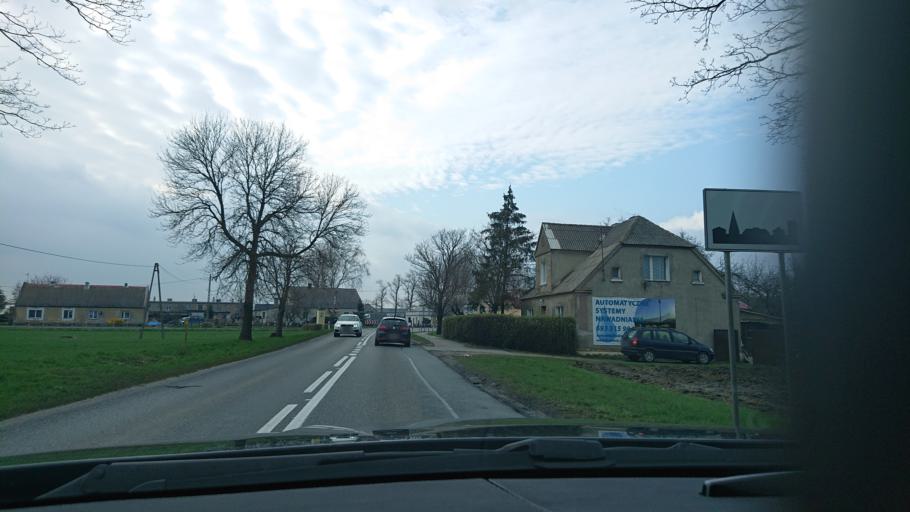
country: PL
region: Greater Poland Voivodeship
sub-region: Powiat gnieznienski
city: Gniezno
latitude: 52.5597
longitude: 17.5280
